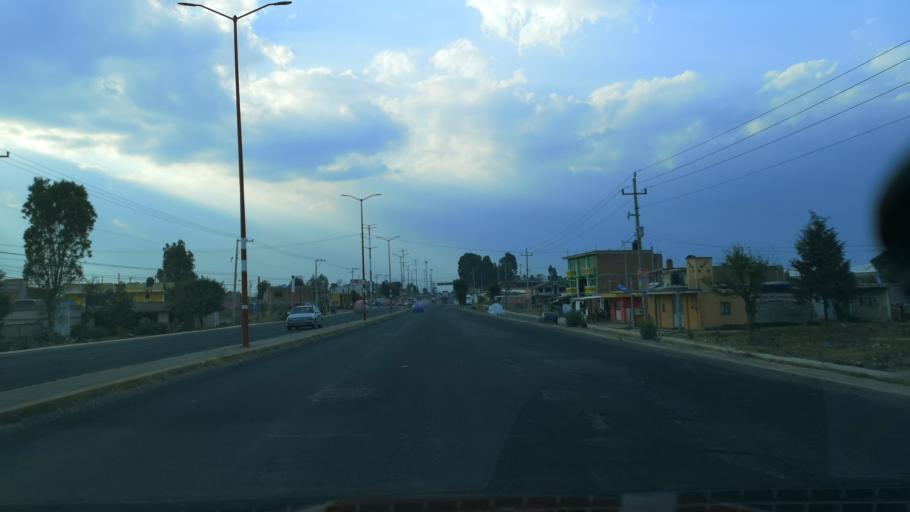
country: MX
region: Puebla
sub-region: Juan C. Bonilla
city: Santa Maria Zacatepec
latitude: 19.1262
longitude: -98.3682
